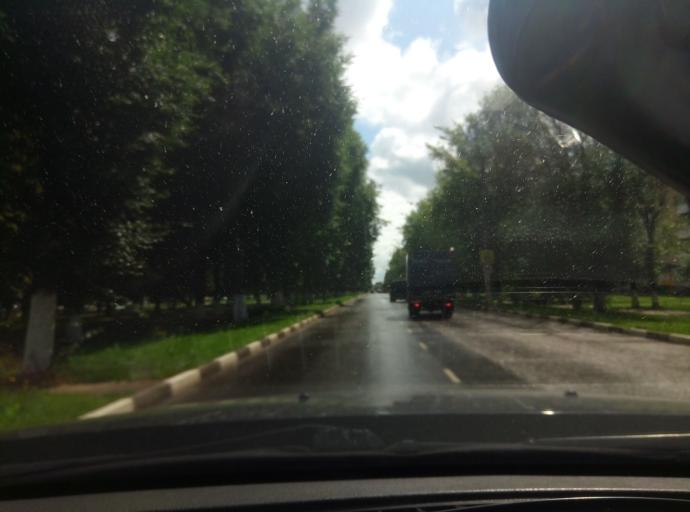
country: RU
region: Tula
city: Novomoskovsk
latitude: 54.0096
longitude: 38.2961
